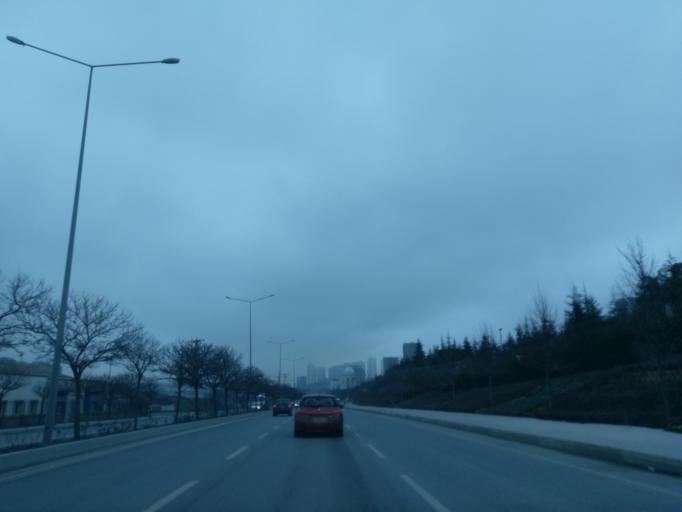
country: TR
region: Istanbul
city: Mahmutbey
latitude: 41.0436
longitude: 28.7737
